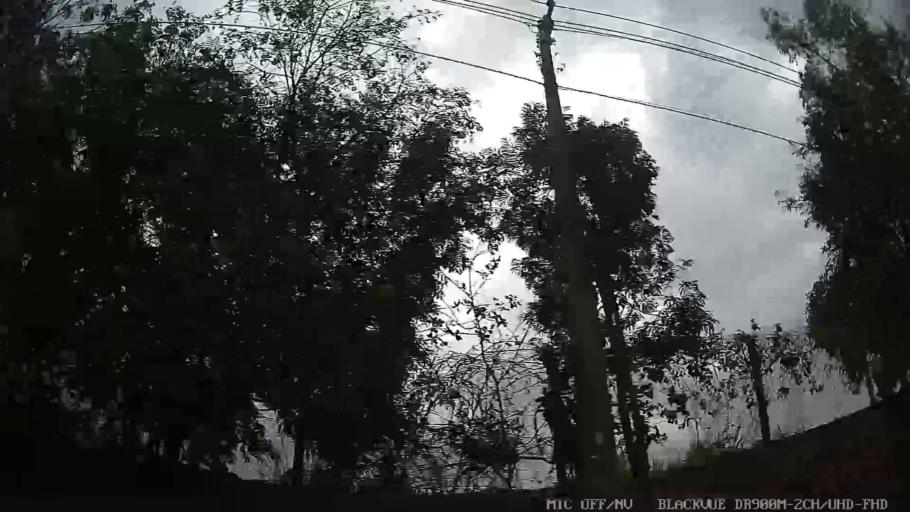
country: BR
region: Sao Paulo
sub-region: Itatiba
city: Itatiba
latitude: -23.0249
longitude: -46.8925
